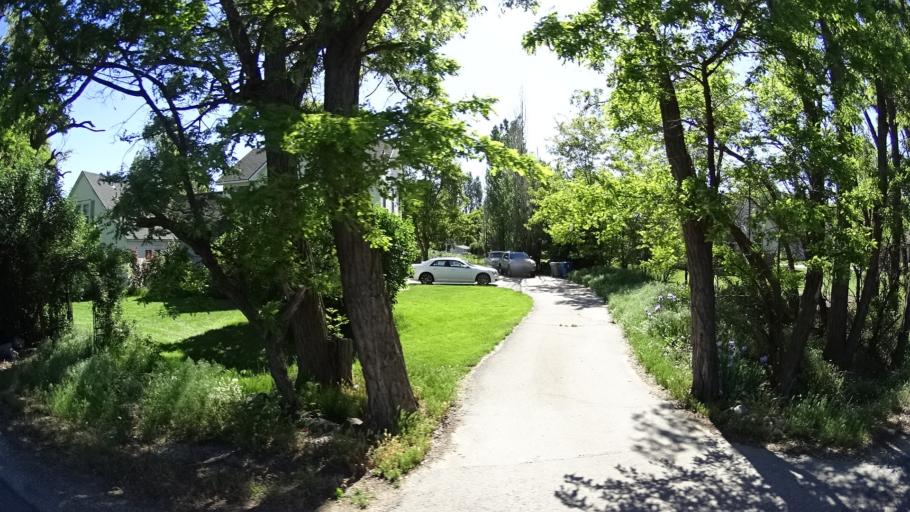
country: US
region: Idaho
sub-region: Ada County
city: Eagle
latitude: 43.6681
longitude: -116.3935
